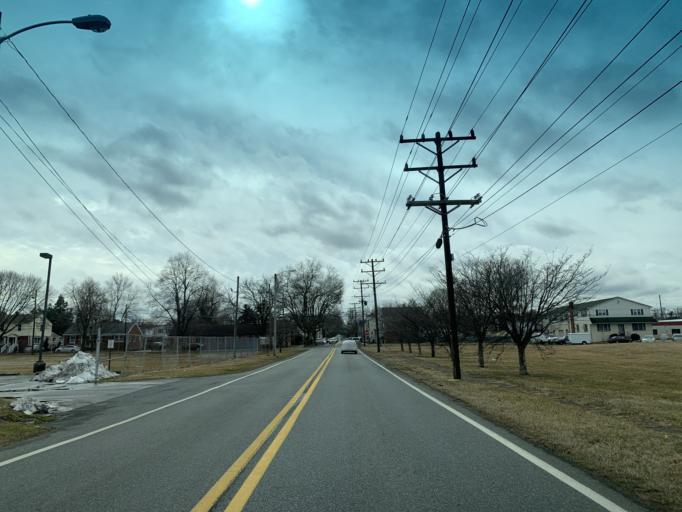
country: US
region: Delaware
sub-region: New Castle County
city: New Castle
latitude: 39.6637
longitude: -75.5648
